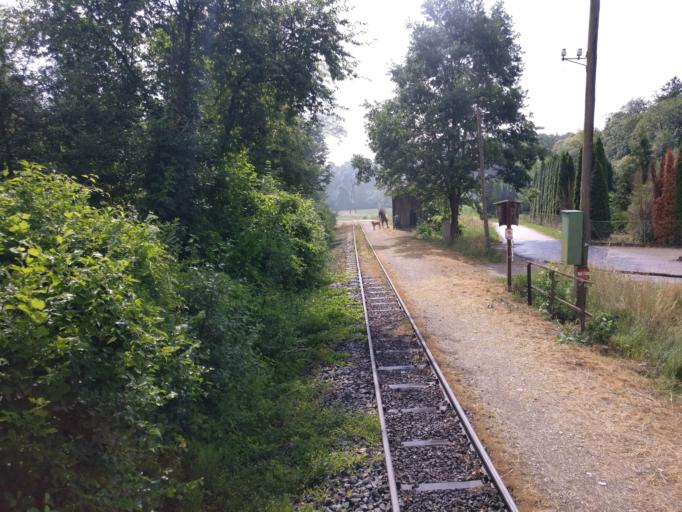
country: AT
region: Upper Austria
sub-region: Politischer Bezirk Steyr-Land
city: Garsten
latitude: 48.0432
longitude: 14.3732
